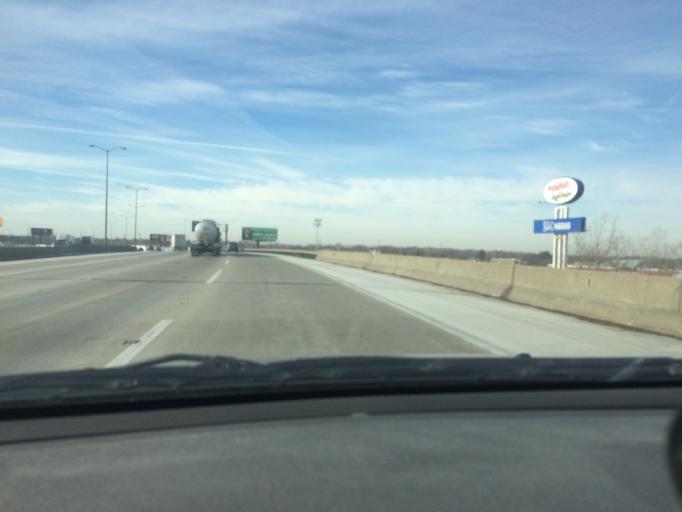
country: US
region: Illinois
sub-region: Cook County
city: Northlake
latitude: 41.9372
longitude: -87.9140
